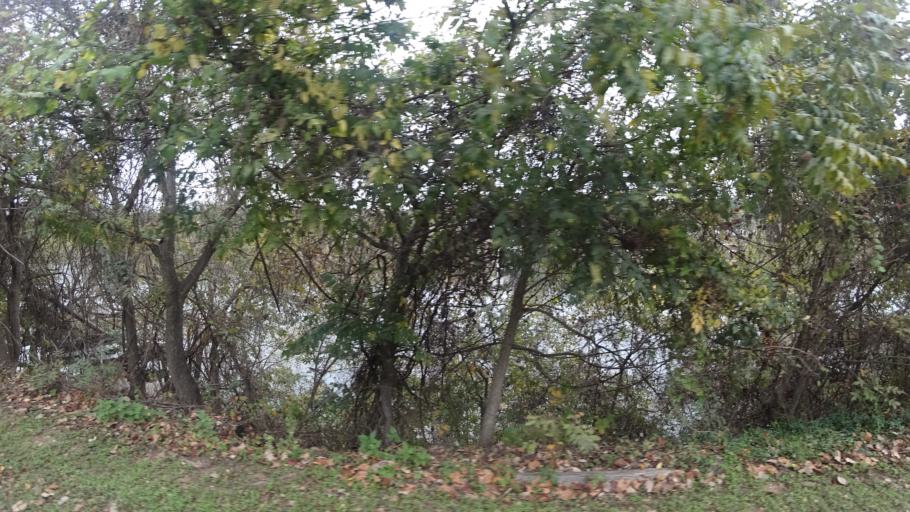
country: US
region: Texas
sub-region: Travis County
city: Hudson Bend
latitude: 30.3739
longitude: -97.9153
